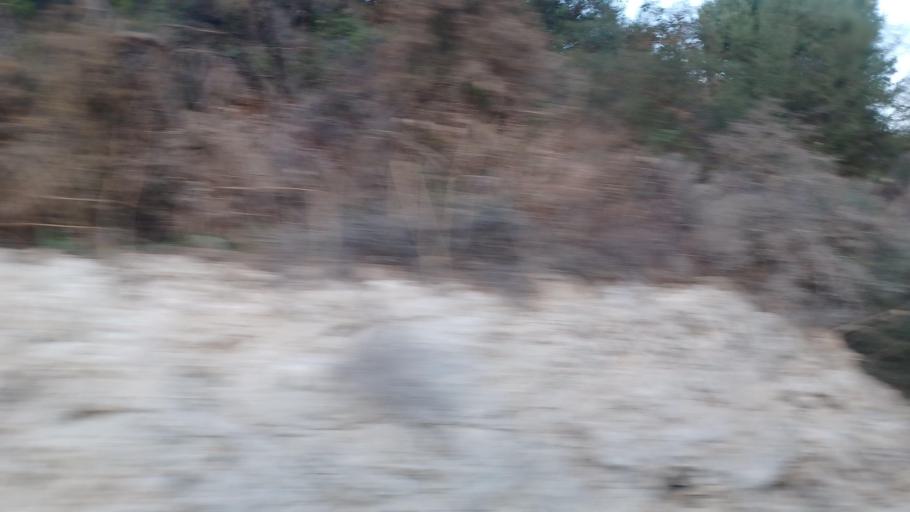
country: CY
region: Pafos
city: Polis
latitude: 34.9864
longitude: 32.4395
